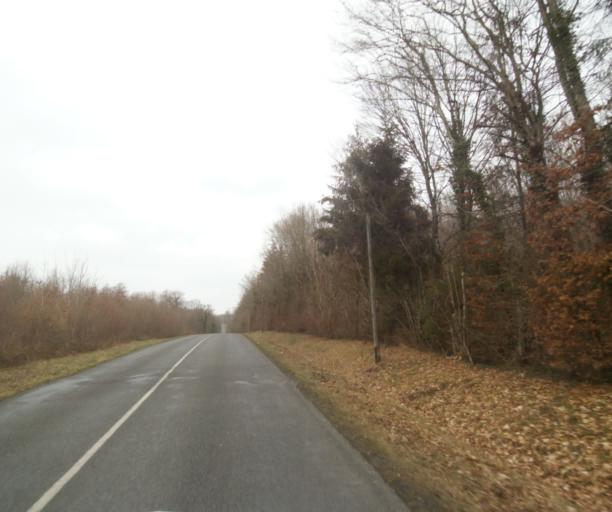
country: FR
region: Champagne-Ardenne
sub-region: Departement de la Haute-Marne
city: Villiers-en-Lieu
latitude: 48.7008
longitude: 4.8951
